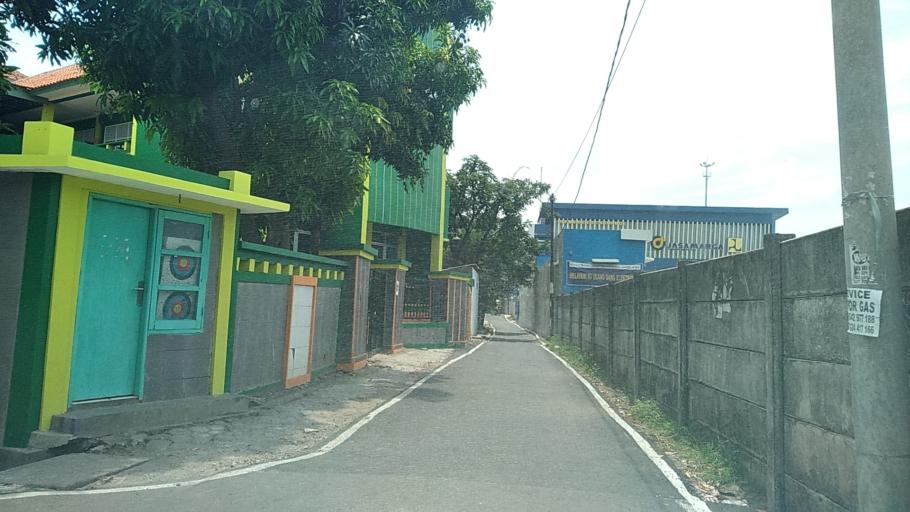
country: ID
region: Central Java
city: Semarang
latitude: -7.0566
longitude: 110.4229
